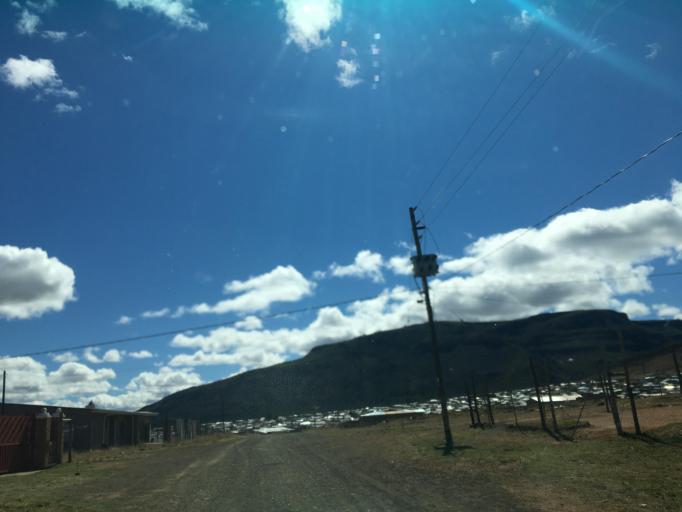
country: ZA
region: Eastern Cape
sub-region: Chris Hani District Municipality
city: Cala
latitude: -31.5401
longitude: 27.6979
